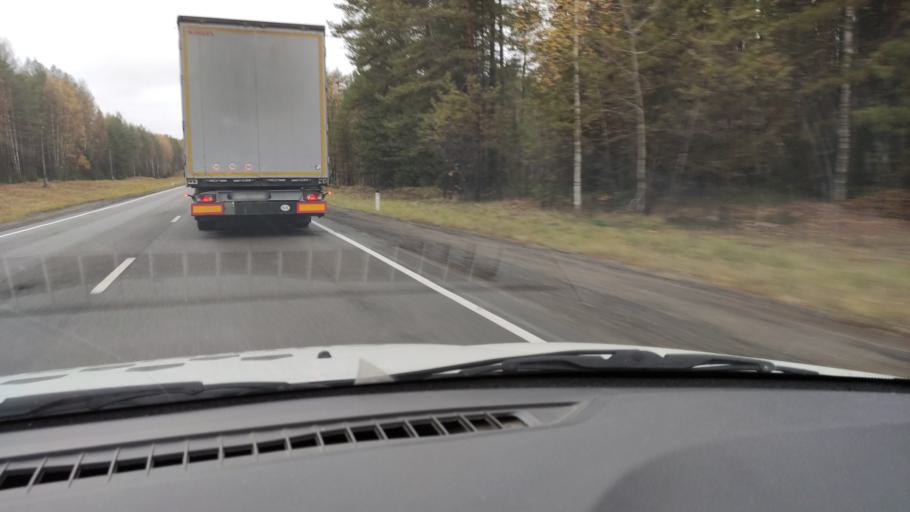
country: RU
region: Kirov
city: Belaya Kholunitsa
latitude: 58.9065
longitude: 50.9703
